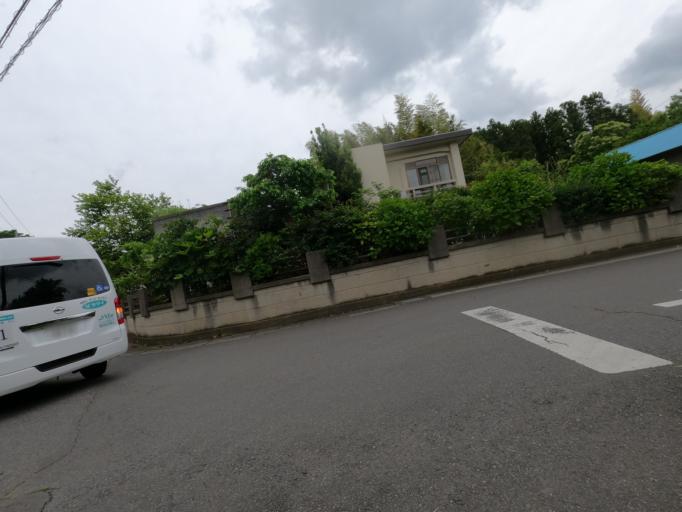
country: JP
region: Ibaraki
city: Moriya
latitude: 35.9537
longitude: 139.9680
